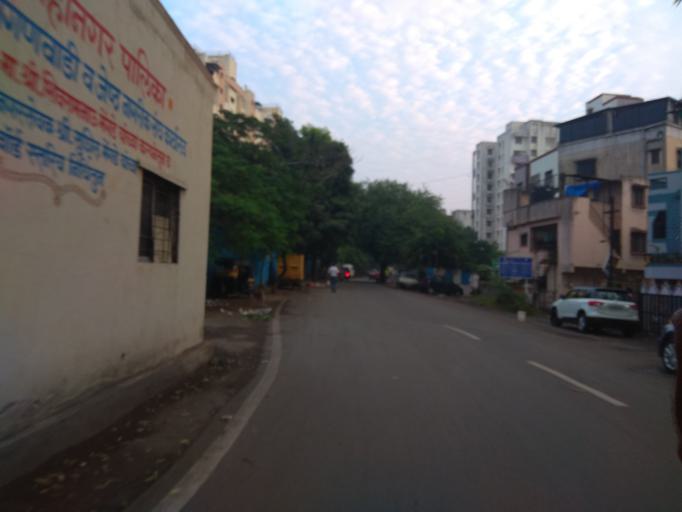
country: IN
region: Maharashtra
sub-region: Pune Division
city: Pune
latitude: 18.4845
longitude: 73.8121
